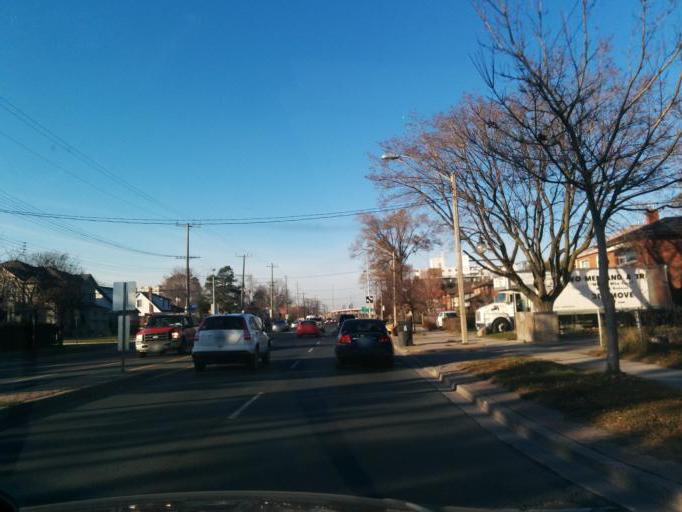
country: CA
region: Ontario
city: Etobicoke
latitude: 43.6061
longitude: -79.5471
